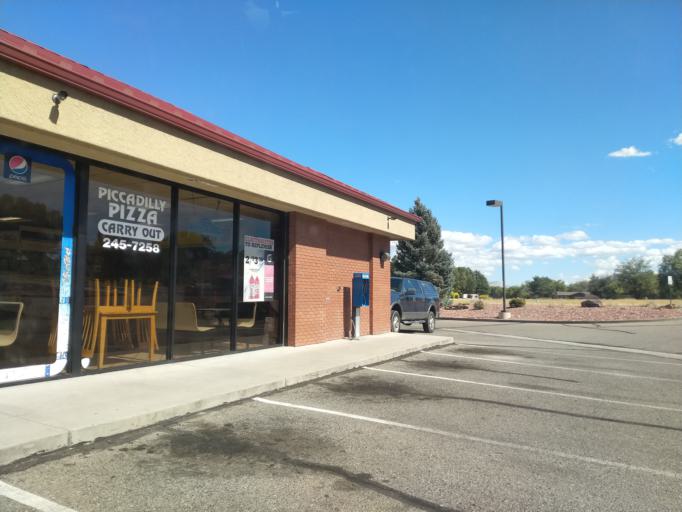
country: US
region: Colorado
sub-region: Mesa County
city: Redlands
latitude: 39.0870
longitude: -108.6505
